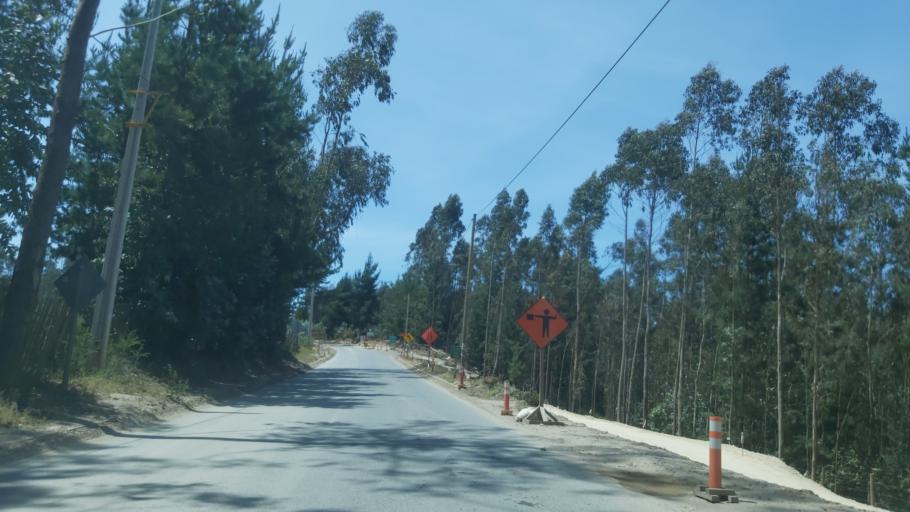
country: CL
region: Maule
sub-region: Provincia de Talca
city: Constitucion
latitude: -35.4400
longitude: -72.4560
